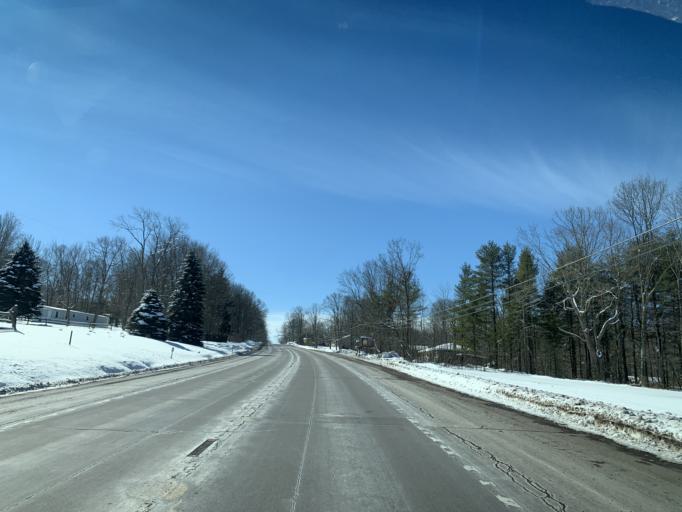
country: US
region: Pennsylvania
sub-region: Somerset County
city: Meyersdale
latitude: 39.7148
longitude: -79.0924
